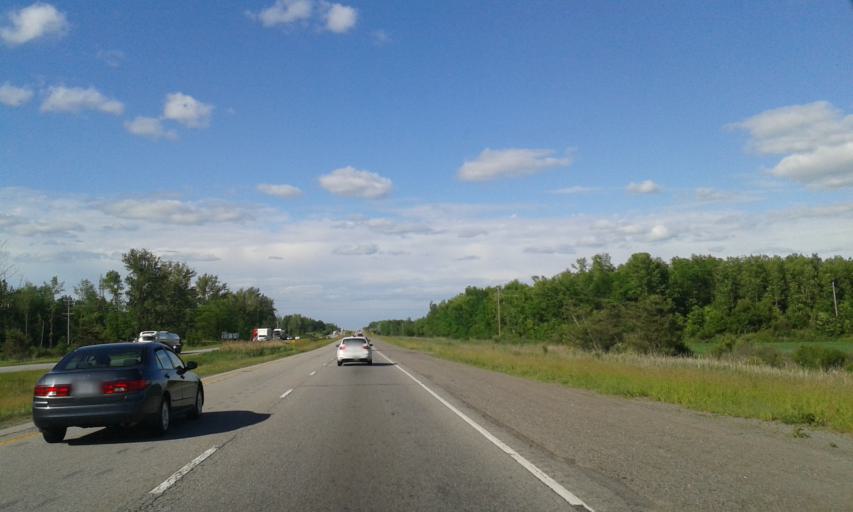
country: CA
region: Ontario
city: Brockville
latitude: 44.6637
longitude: -75.6129
